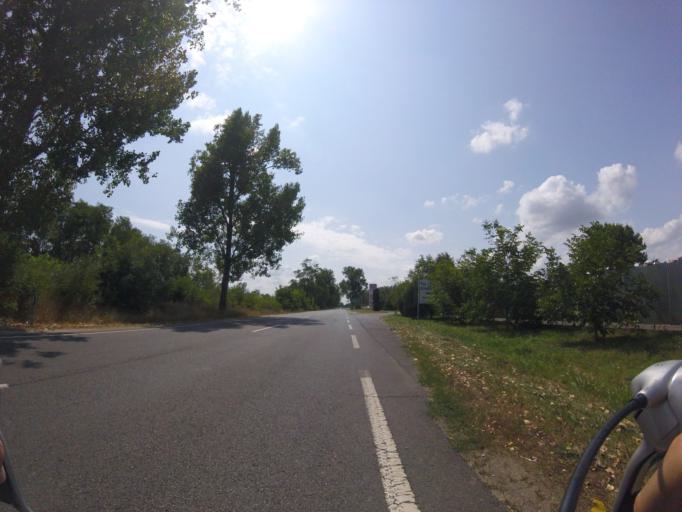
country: HU
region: Szabolcs-Szatmar-Bereg
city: Nyirbogdany
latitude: 48.0457
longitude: 21.8676
